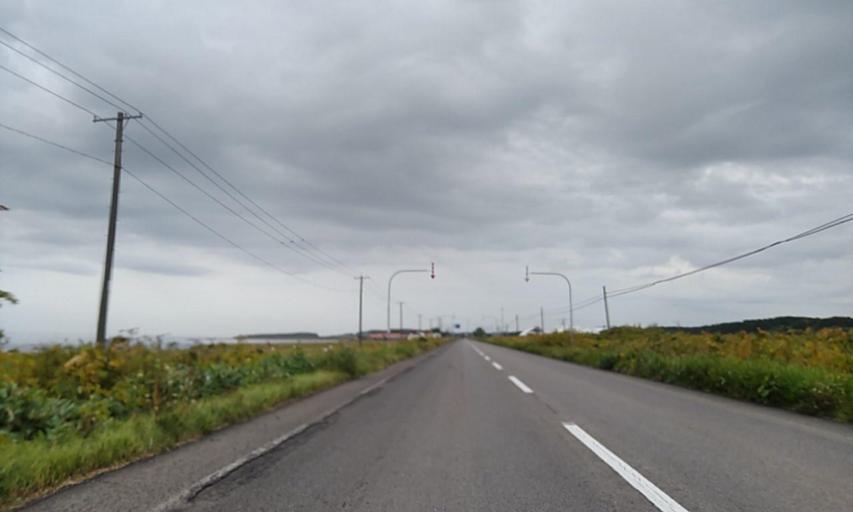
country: JP
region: Hokkaido
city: Nayoro
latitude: 44.6370
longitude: 142.9043
